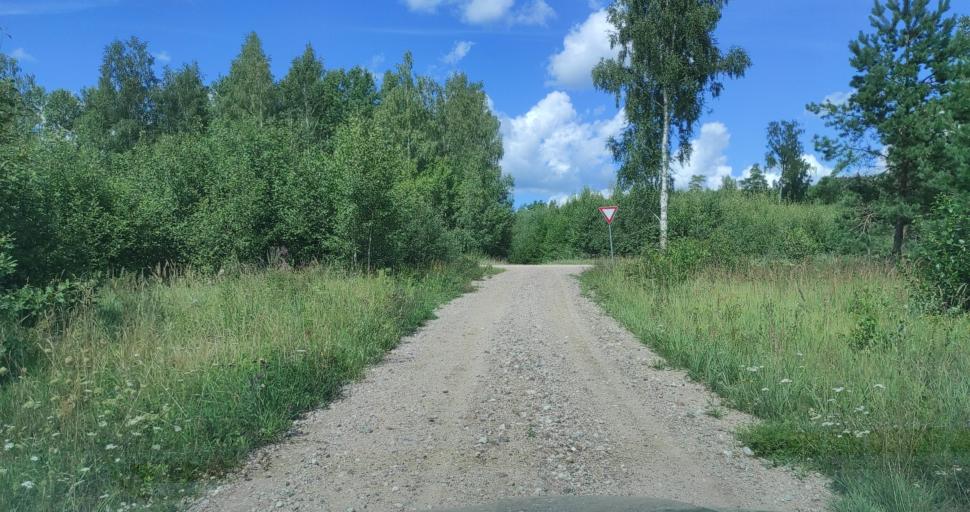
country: LV
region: Alsunga
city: Alsunga
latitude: 57.0313
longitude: 21.6960
